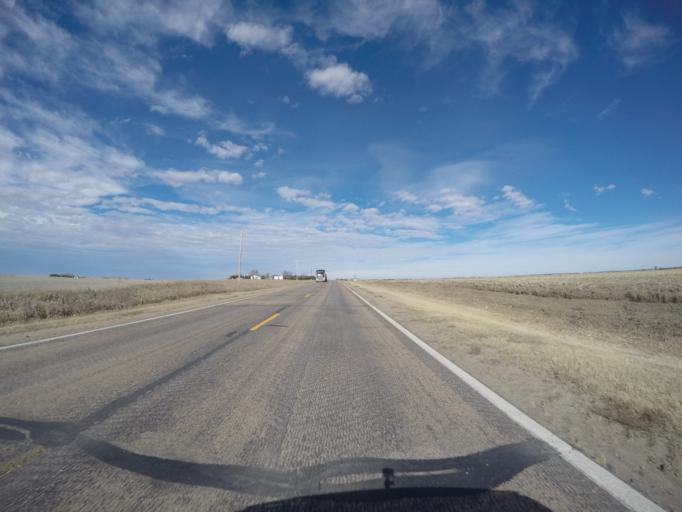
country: US
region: Nebraska
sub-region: Franklin County
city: Franklin
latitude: 40.2717
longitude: -98.9524
